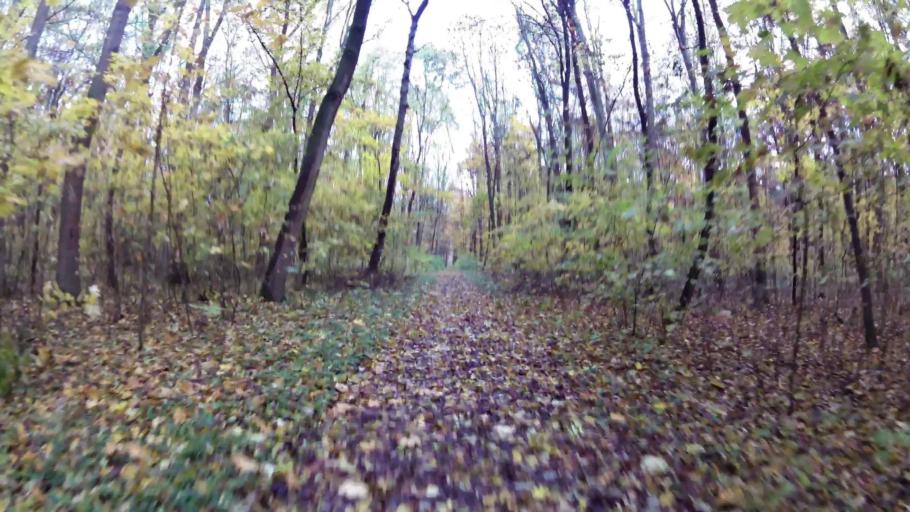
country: DE
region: Thuringia
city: Weimar
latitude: 50.9813
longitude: 11.3469
